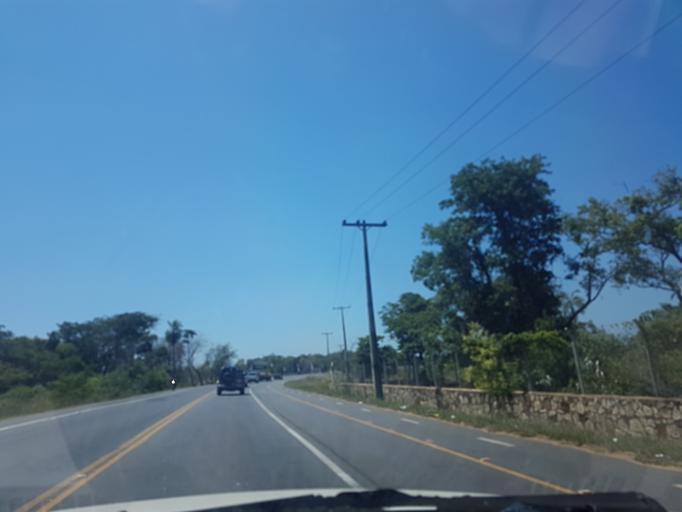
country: PY
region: Cordillera
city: San Bernardino
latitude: -25.2723
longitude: -57.3184
